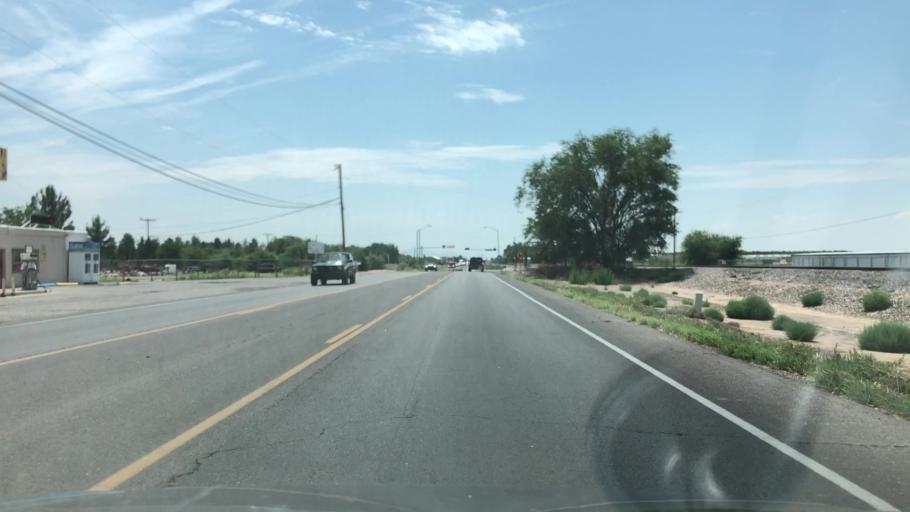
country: US
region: New Mexico
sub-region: Dona Ana County
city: University Park
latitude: 32.2633
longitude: -106.7591
